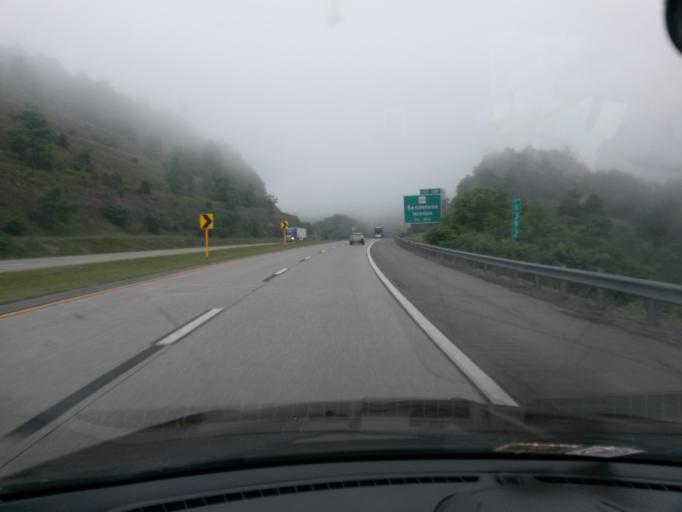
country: US
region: West Virginia
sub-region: Summers County
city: Hinton
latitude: 37.7858
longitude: -80.8812
